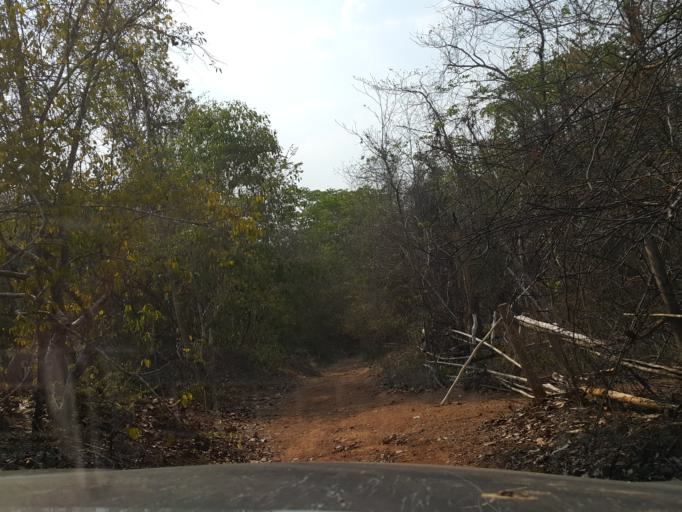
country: TH
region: Lampang
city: Mae Phrik
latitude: 17.5229
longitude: 98.9964
